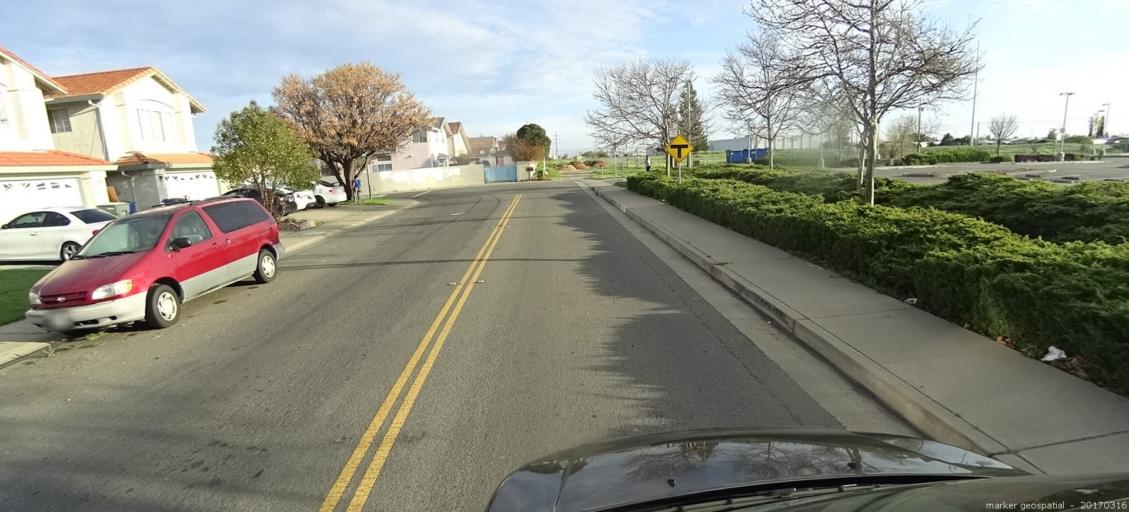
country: US
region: California
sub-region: Sacramento County
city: Parkway
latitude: 38.4981
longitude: -121.4738
